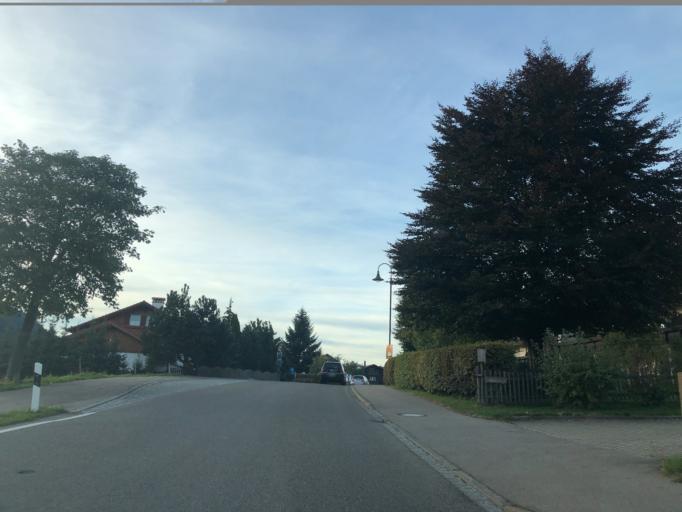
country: DE
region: Bavaria
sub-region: Swabia
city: Pfronten
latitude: 47.5929
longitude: 10.5563
